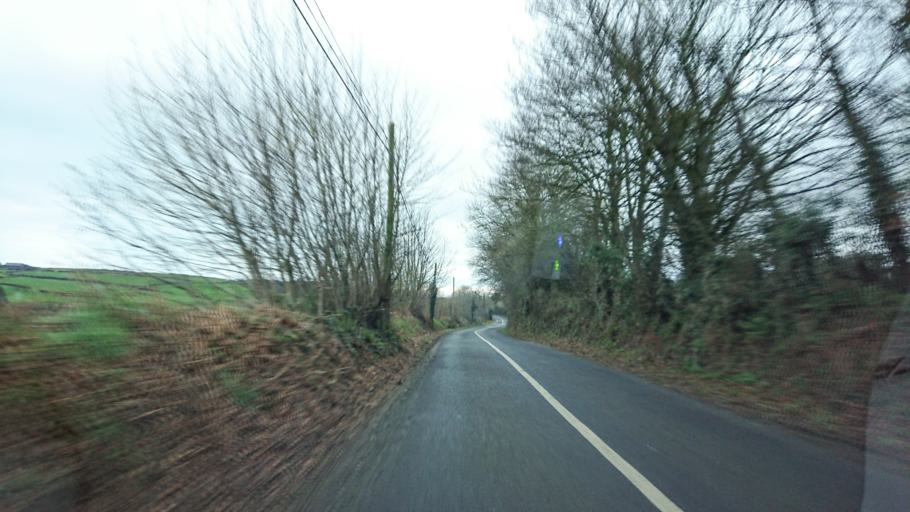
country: IE
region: Munster
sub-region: Waterford
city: Portlaw
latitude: 52.1652
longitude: -7.3887
